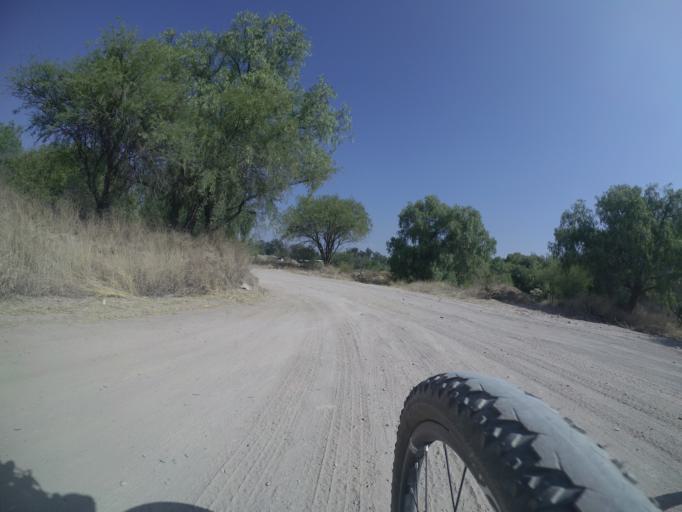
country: MX
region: Aguascalientes
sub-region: Jesus Maria
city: Paseos de las Haciendas [Fraccionamiento]
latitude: 21.9990
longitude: -102.3354
